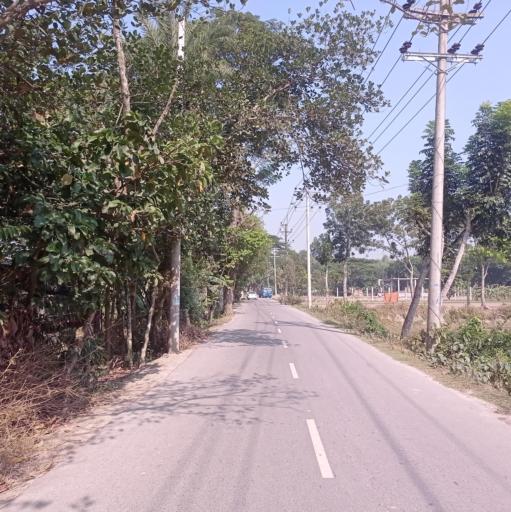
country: BD
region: Dhaka
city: Narsingdi
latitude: 24.0640
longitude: 90.6901
